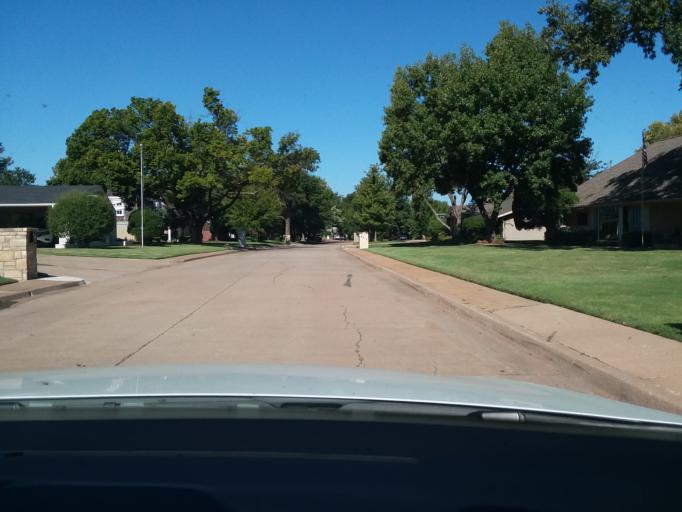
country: US
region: Oklahoma
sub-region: Oklahoma County
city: The Village
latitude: 35.6000
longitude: -97.5715
